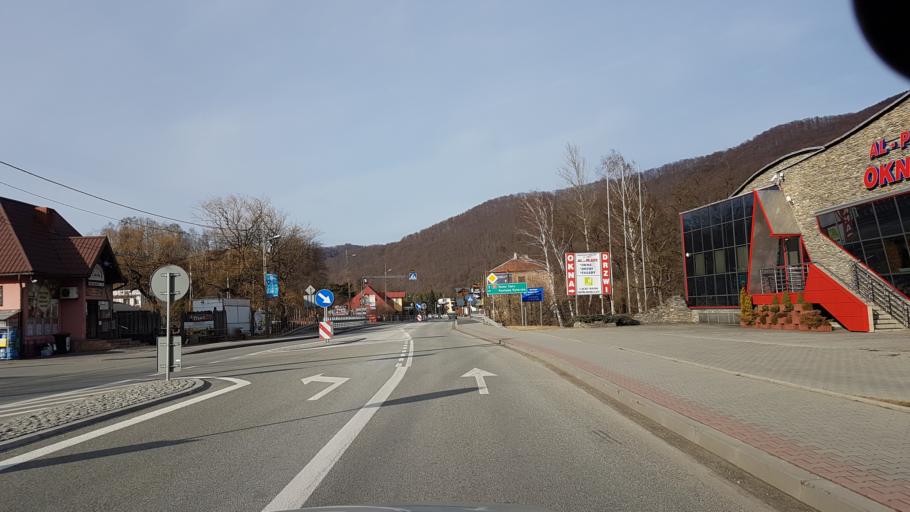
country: PL
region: Lesser Poland Voivodeship
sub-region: Powiat nowosadecki
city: Rytro
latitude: 49.4883
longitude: 20.6815
